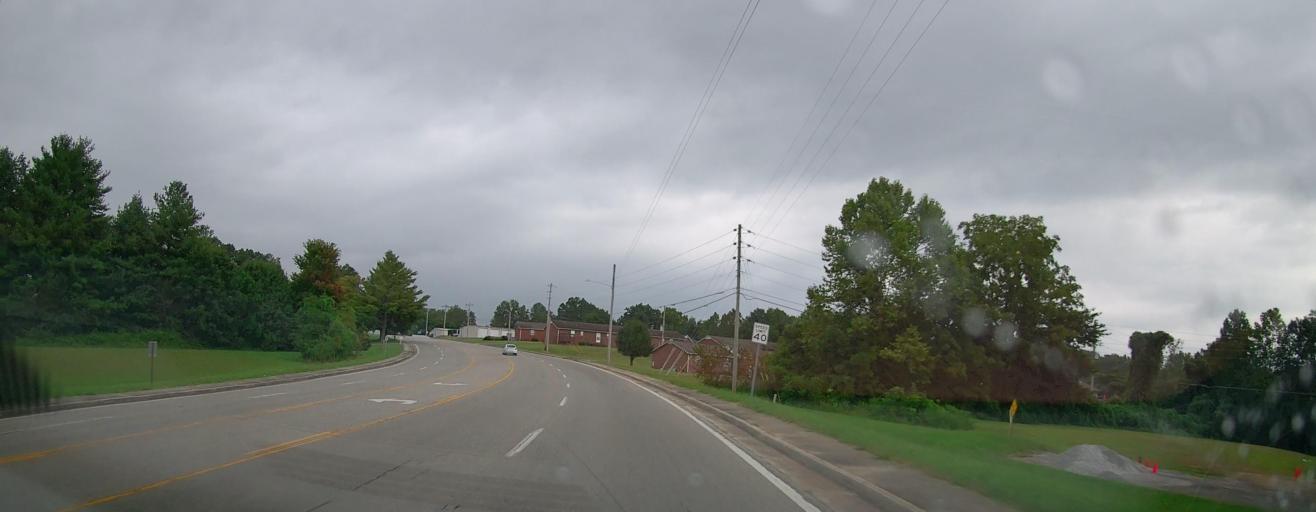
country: US
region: Tennessee
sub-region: Coffee County
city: Manchester
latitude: 35.4902
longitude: -86.0888
